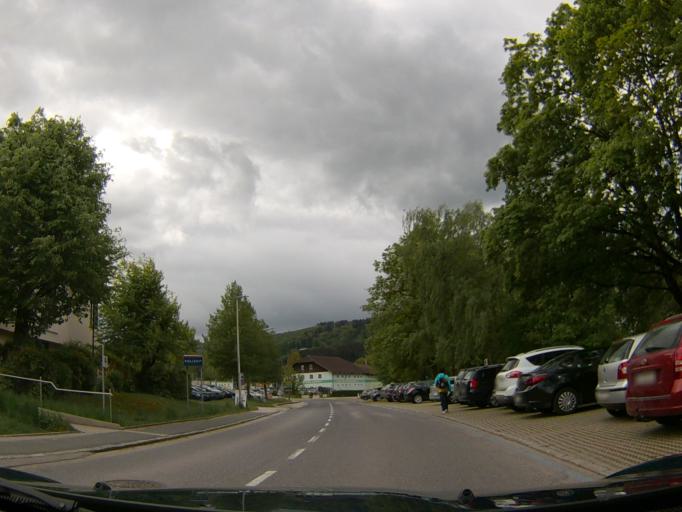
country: AT
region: Upper Austria
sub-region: Politischer Bezirk Vocklabruck
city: Seewalchen
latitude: 47.9458
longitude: 13.5945
